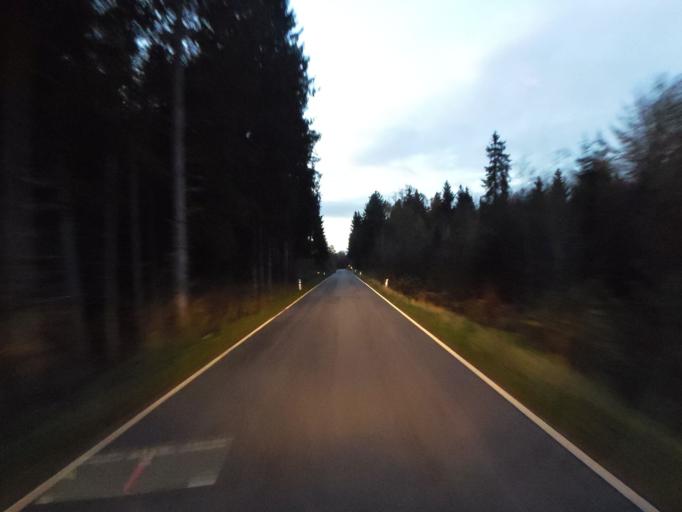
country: DE
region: Bavaria
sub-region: Upper Bavaria
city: Hohenkirchen-Siegertsbrunn
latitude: 47.9756
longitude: 11.7228
